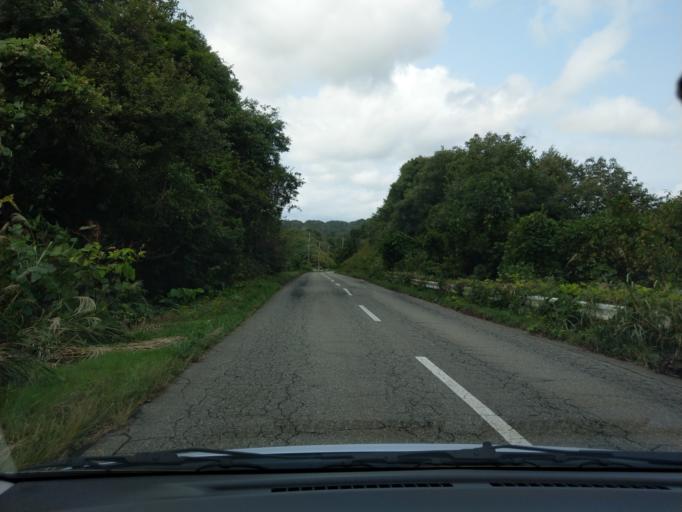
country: JP
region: Akita
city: Omagari
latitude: 39.4717
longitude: 140.3156
